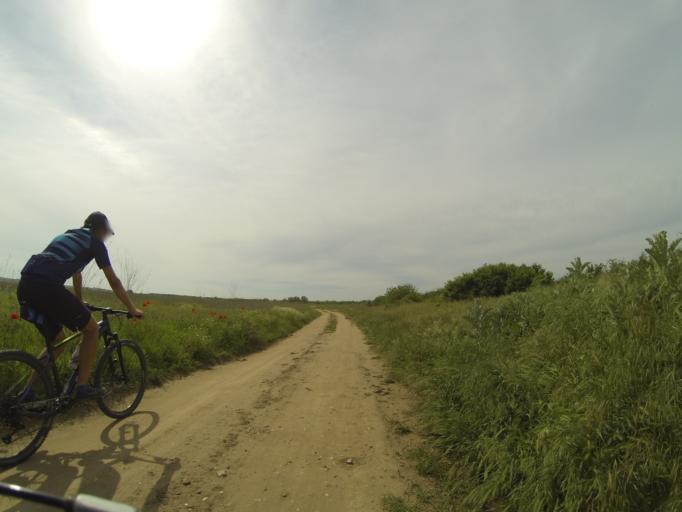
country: RO
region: Dolj
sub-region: Comuna Malu Mare
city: Preajba
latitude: 44.2667
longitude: 23.8634
